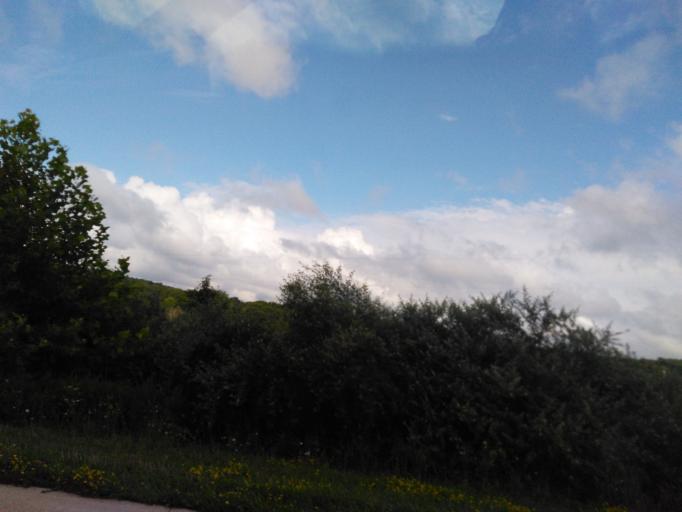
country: US
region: Missouri
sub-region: Jefferson County
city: Hillsboro
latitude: 38.2975
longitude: -90.5427
